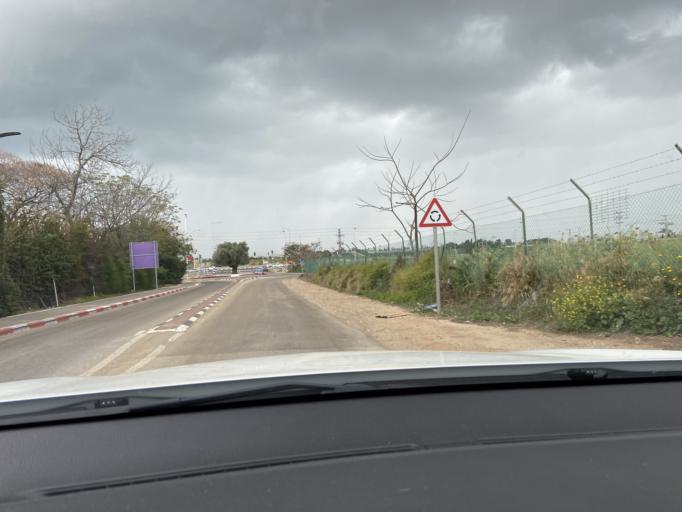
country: IL
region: Northern District
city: El Mazra`a
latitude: 32.9778
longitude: 35.0960
